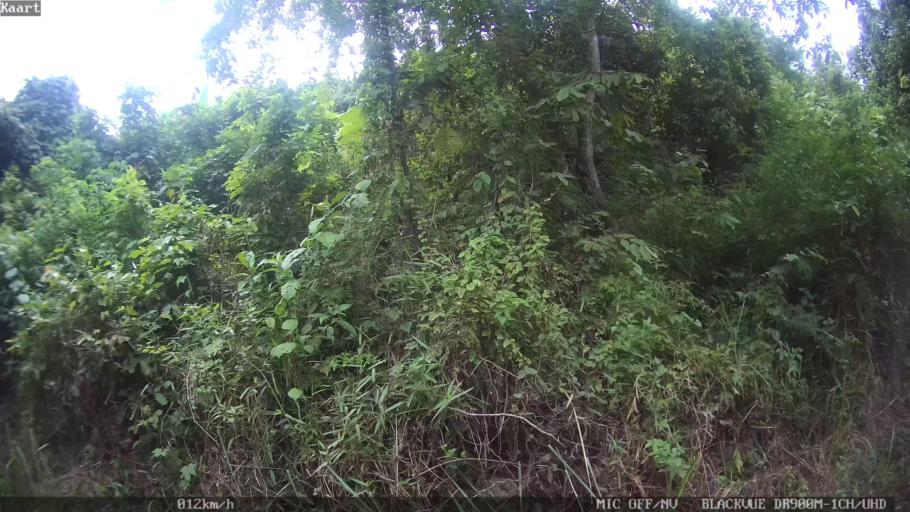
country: ID
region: Lampung
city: Panjang
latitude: -5.4319
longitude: 105.3092
